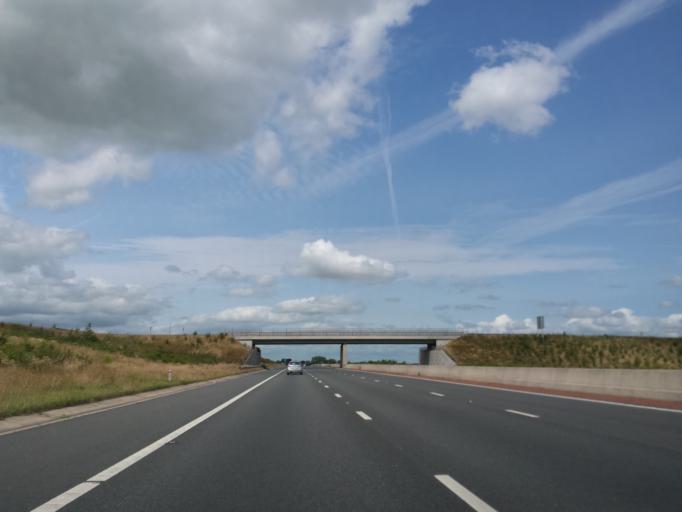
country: GB
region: England
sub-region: North Yorkshire
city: Ripon
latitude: 54.2378
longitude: -1.4979
